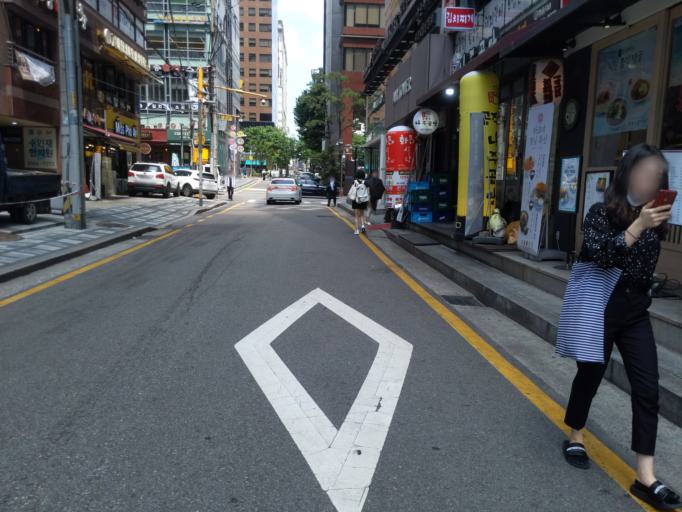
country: KR
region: Seoul
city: Seoul
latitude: 37.4943
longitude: 127.0280
